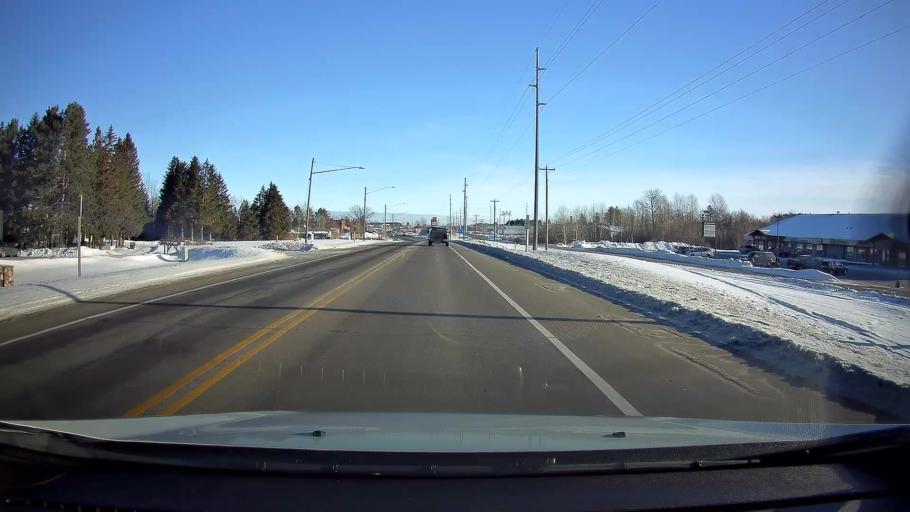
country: US
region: Wisconsin
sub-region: Sawyer County
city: Hayward
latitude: 46.0073
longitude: -91.4926
